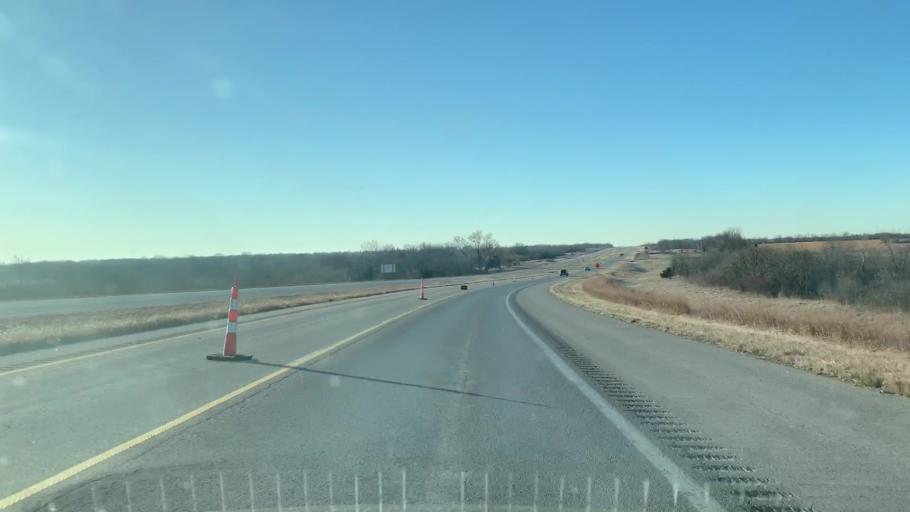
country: US
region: Kansas
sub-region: Bourbon County
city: Fort Scott
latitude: 37.7661
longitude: -94.7051
